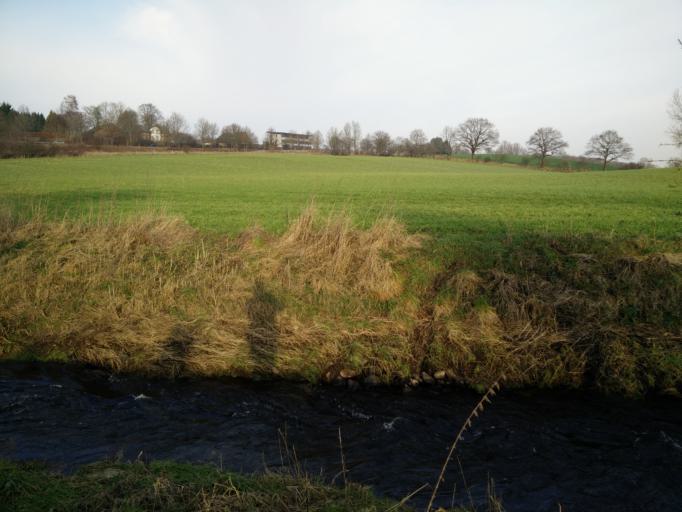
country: DE
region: Schleswig-Holstein
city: Neritz
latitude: 53.7837
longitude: 10.2935
